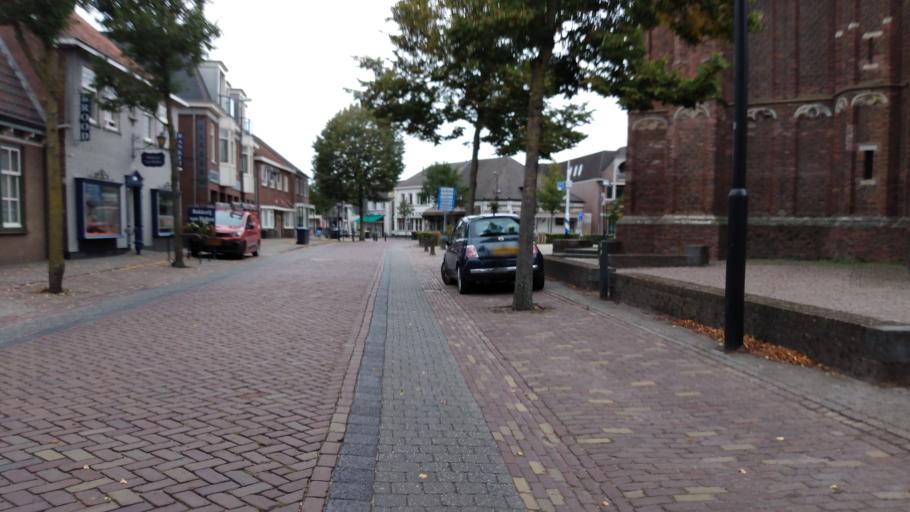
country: NL
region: North Brabant
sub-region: Gemeente Oisterwijk
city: Oisterwijk
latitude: 51.5445
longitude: 5.1829
